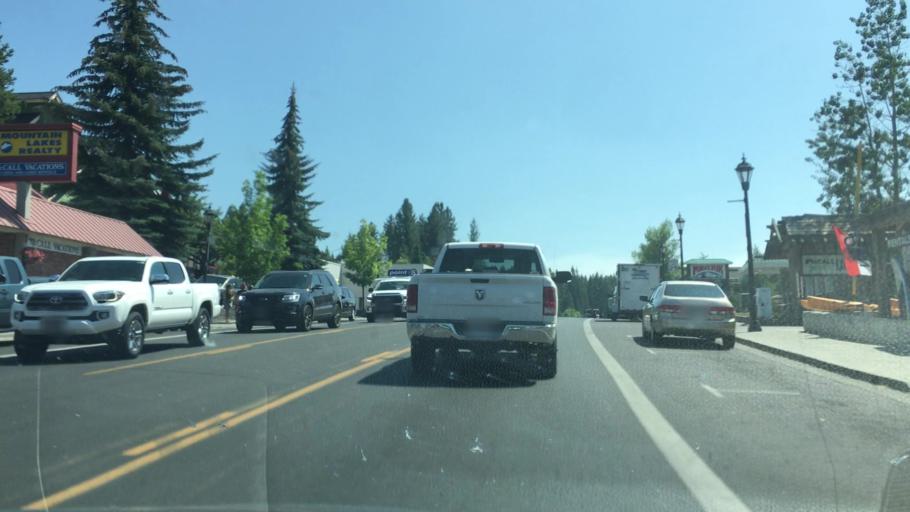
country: US
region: Idaho
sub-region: Valley County
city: McCall
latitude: 44.9092
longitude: -116.0977
